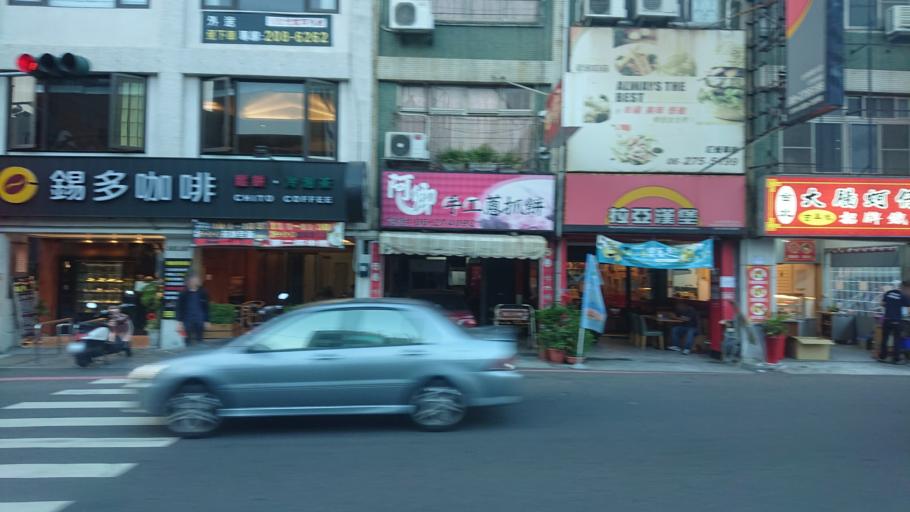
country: TW
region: Taiwan
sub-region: Tainan
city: Tainan
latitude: 23.0112
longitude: 120.2259
